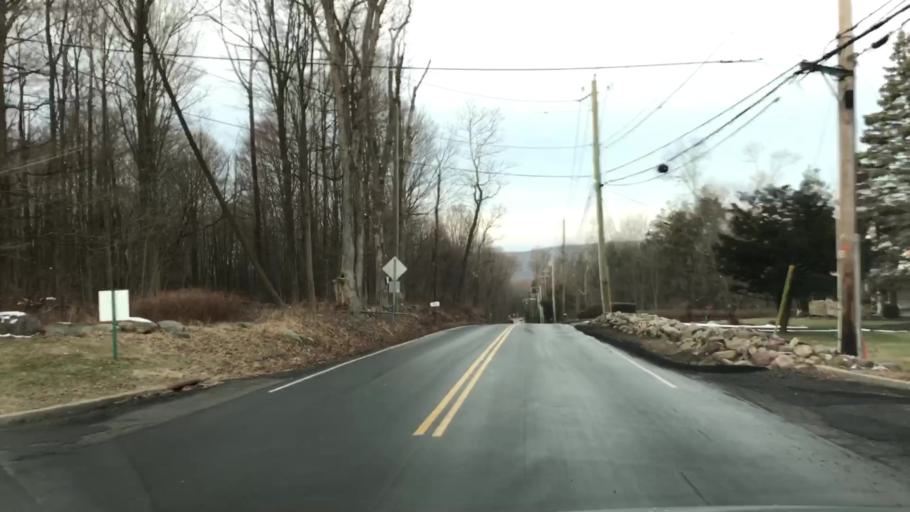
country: US
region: New York
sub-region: Rockland County
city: Viola
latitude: 41.1364
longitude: -74.0904
